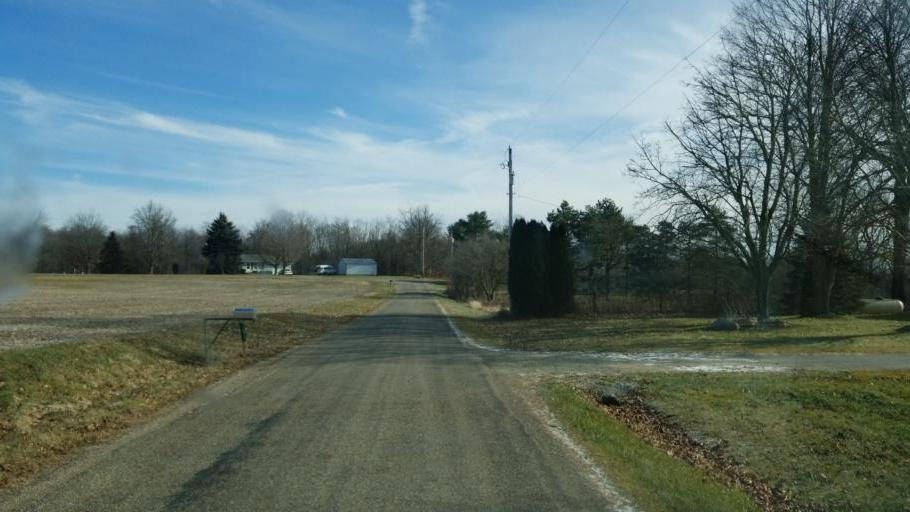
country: US
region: Ohio
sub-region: Sandusky County
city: Bellville
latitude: 40.5719
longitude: -82.5708
